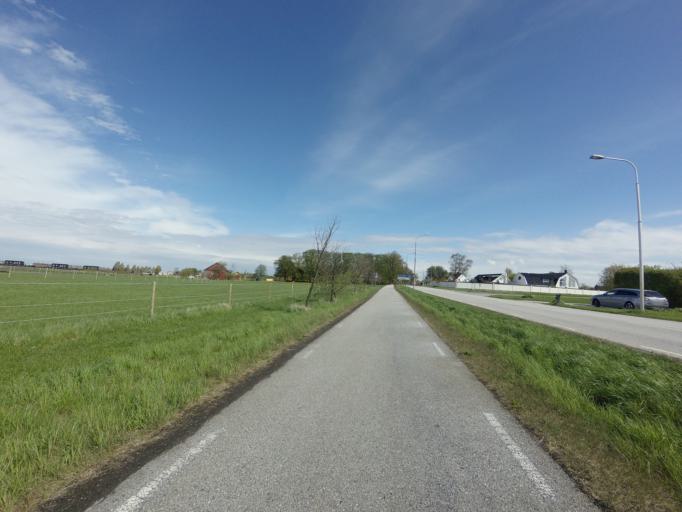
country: SE
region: Skane
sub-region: Malmo
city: Tygelsjo
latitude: 55.5117
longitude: 12.9952
